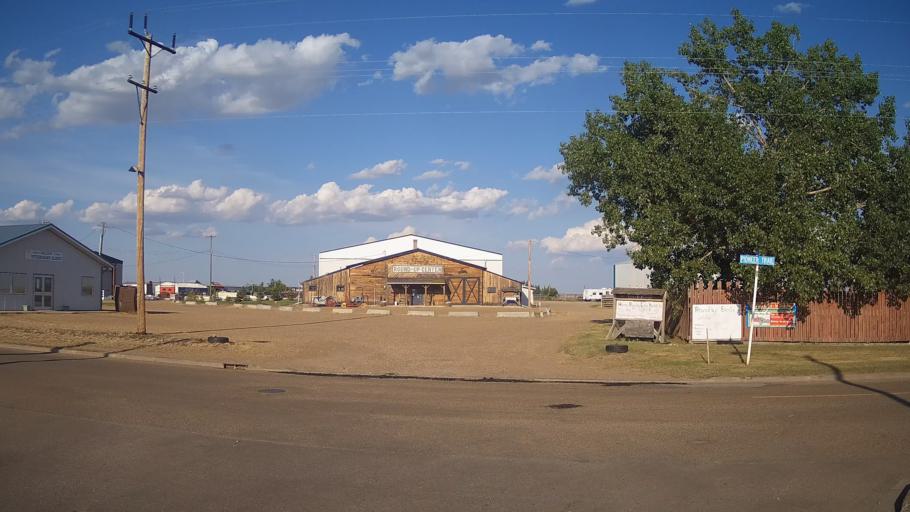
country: CA
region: Alberta
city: Hanna
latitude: 51.6449
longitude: -111.9187
